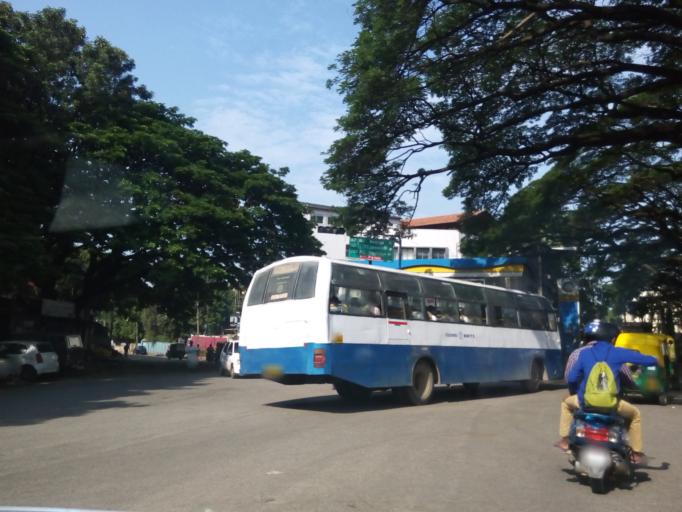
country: IN
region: Karnataka
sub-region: Bangalore Urban
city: Bangalore
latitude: 12.9921
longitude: 77.6043
